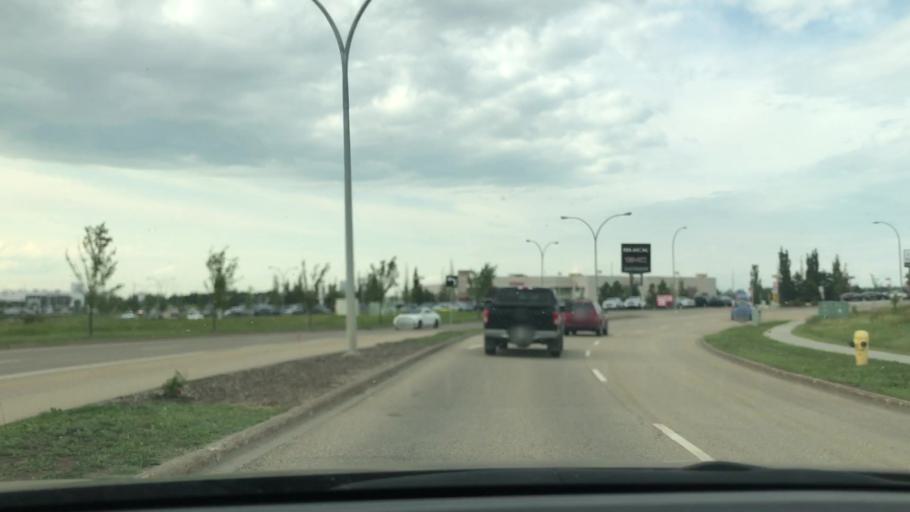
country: CA
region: Alberta
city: Sherwood Park
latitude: 53.5430
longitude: -113.3248
